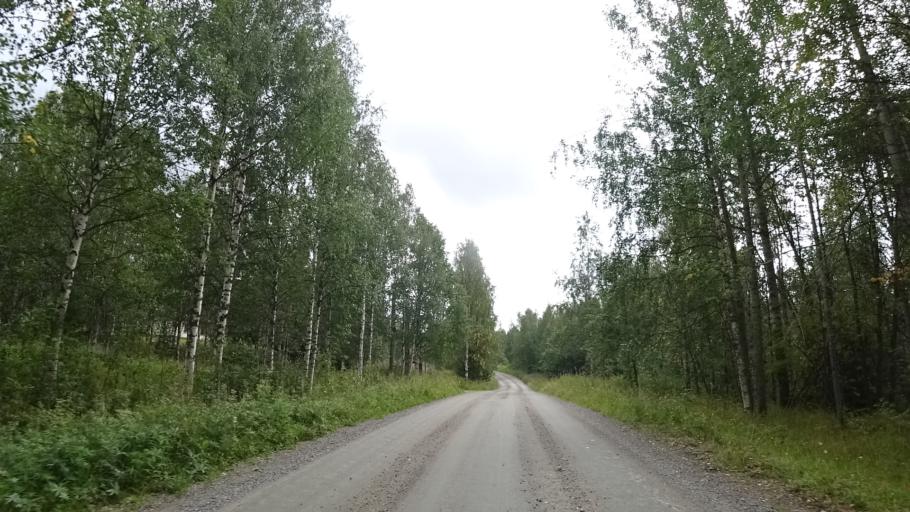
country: FI
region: North Karelia
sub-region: Joensuu
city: Ilomantsi
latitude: 62.9330
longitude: 31.3069
